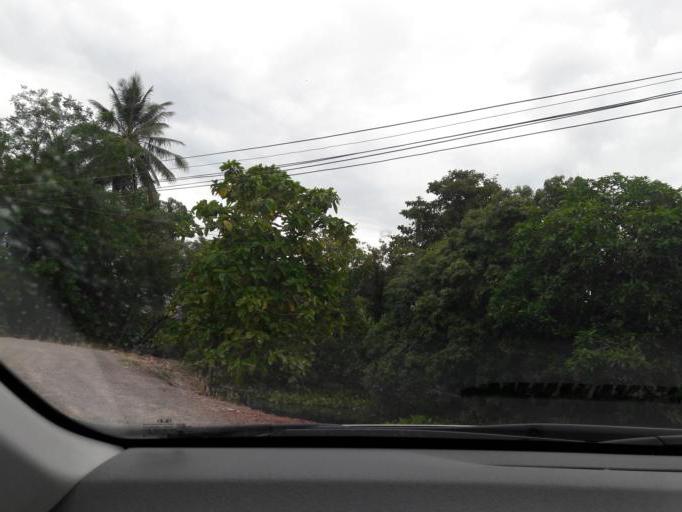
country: TH
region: Ratchaburi
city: Damnoen Saduak
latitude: 13.5560
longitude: 99.9728
